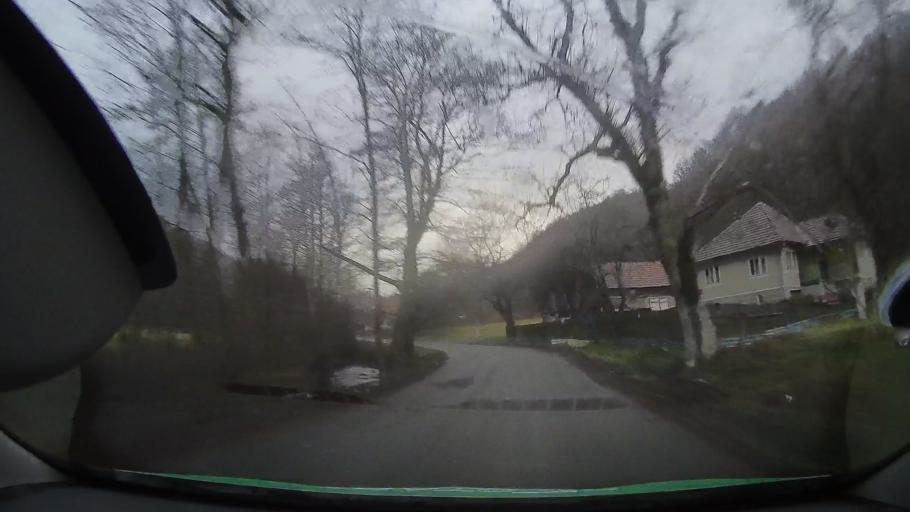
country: RO
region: Hunedoara
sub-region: Comuna Ribita
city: Ribita
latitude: 46.2624
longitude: 22.7433
